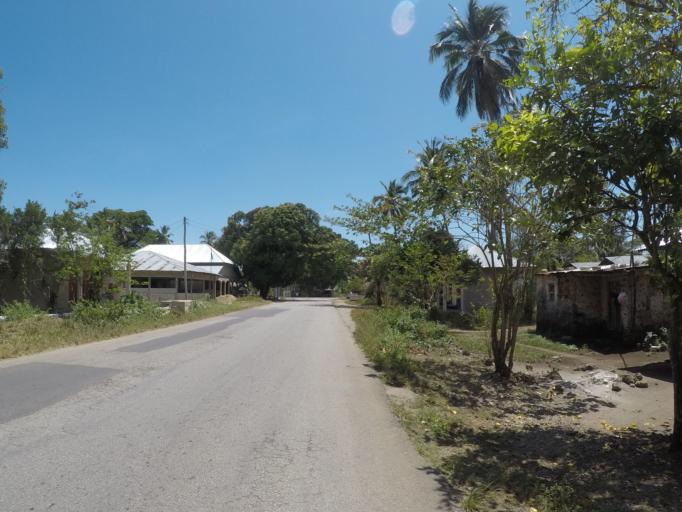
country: TZ
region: Zanzibar Central/South
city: Nganane
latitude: -6.2886
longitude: 39.4391
